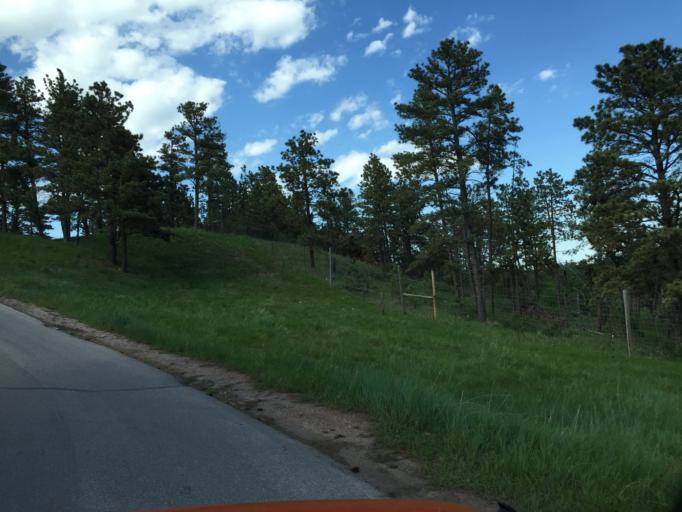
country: US
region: South Dakota
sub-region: Pennington County
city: Colonial Pine Hills
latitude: 43.9761
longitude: -103.2943
